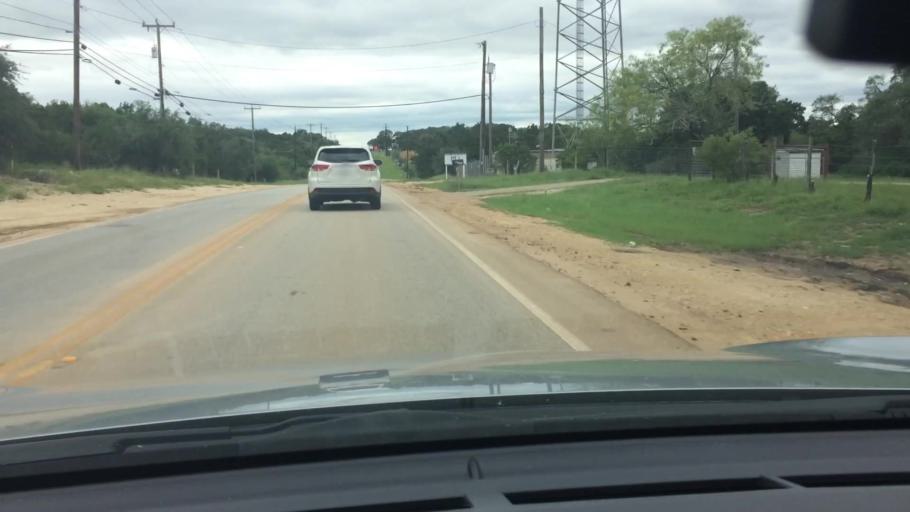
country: US
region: Texas
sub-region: Comal County
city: Garden Ridge
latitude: 29.6394
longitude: -98.3775
